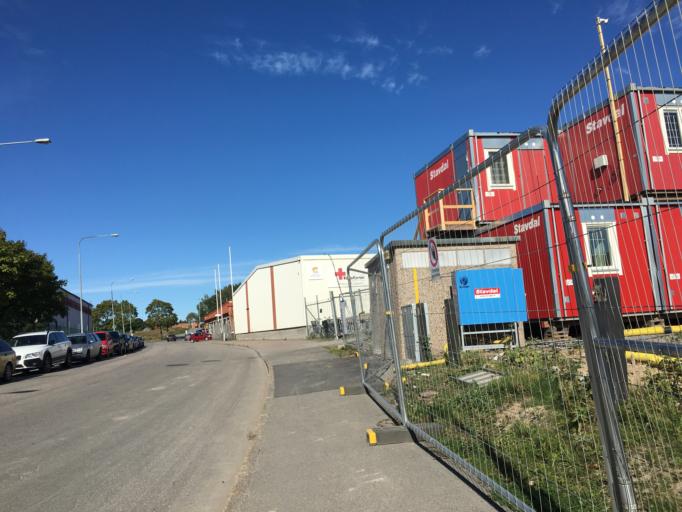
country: SE
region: Uppsala
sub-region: Uppsala Kommun
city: Uppsala
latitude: 59.8532
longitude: 17.6702
